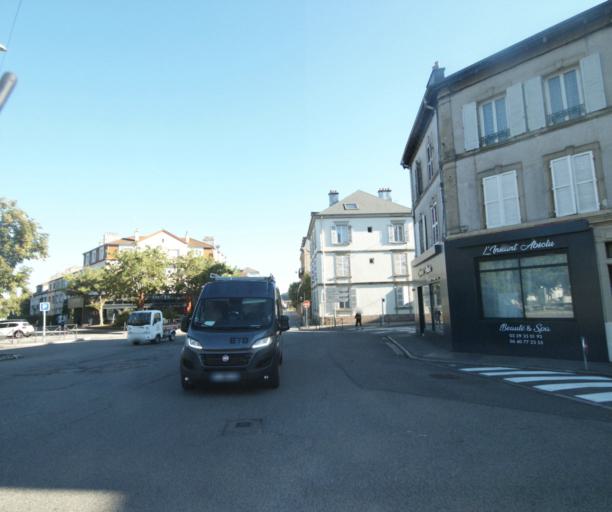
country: FR
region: Lorraine
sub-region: Departement des Vosges
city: Epinal
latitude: 48.1668
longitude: 6.4517
